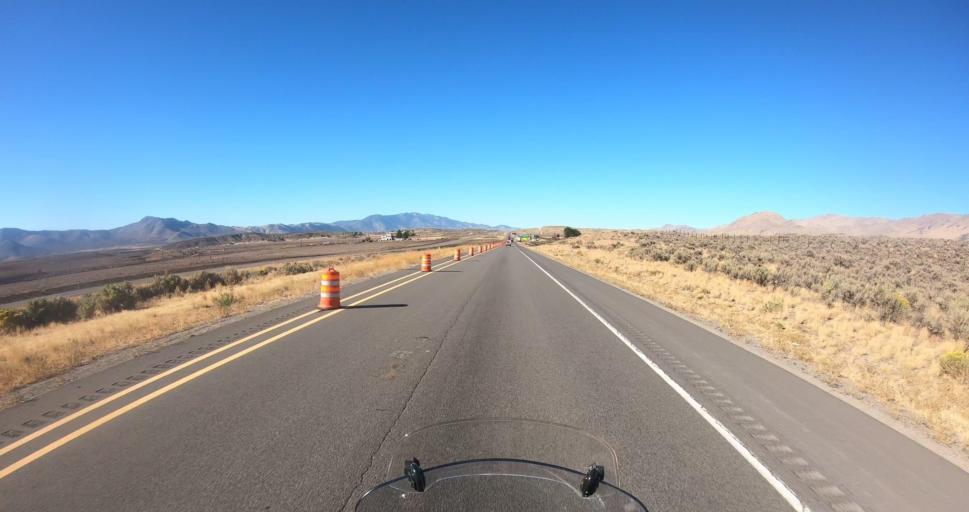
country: US
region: Nevada
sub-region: Washoe County
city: Cold Springs
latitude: 39.7253
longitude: -120.0380
